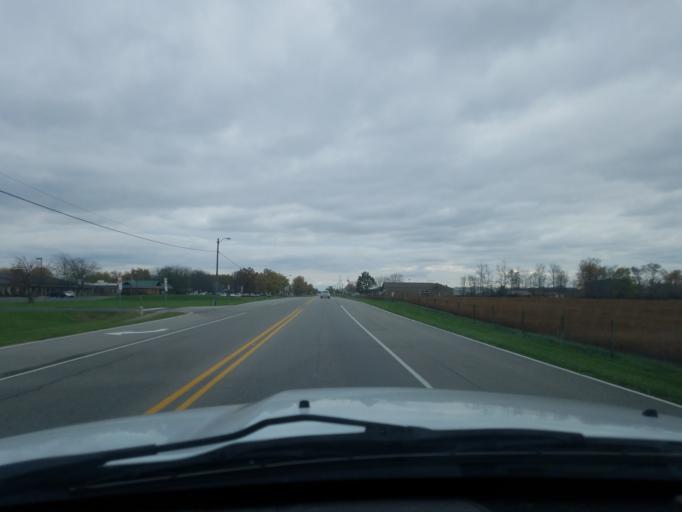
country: US
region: Indiana
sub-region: Bartholomew County
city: Hope
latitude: 39.2946
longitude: -85.7715
